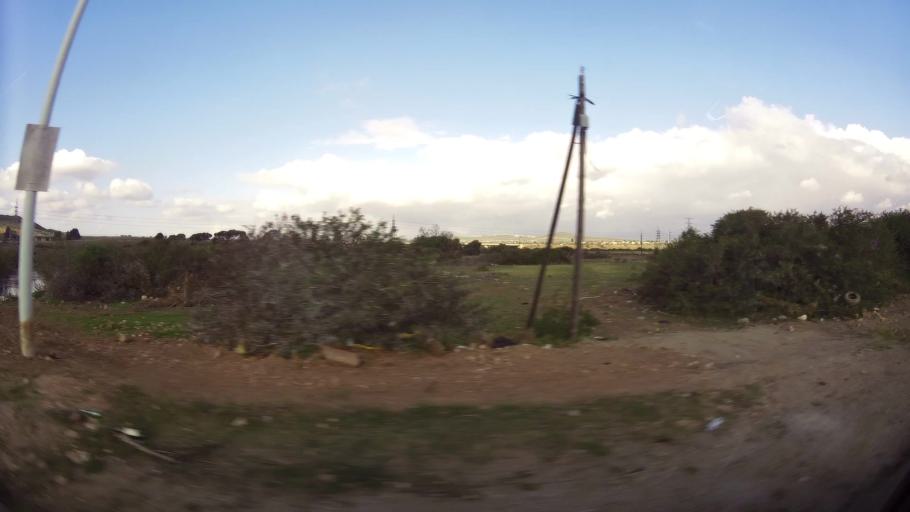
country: ZA
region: Eastern Cape
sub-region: Nelson Mandela Bay Metropolitan Municipality
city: Uitenhage
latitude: -33.7831
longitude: 25.4278
